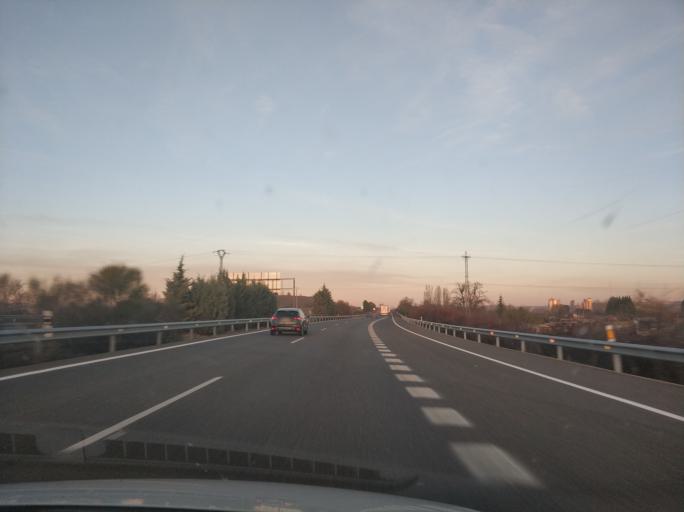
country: ES
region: Castille and Leon
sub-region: Provincia de Palencia
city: Venta de Banos
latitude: 41.9375
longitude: -4.4932
